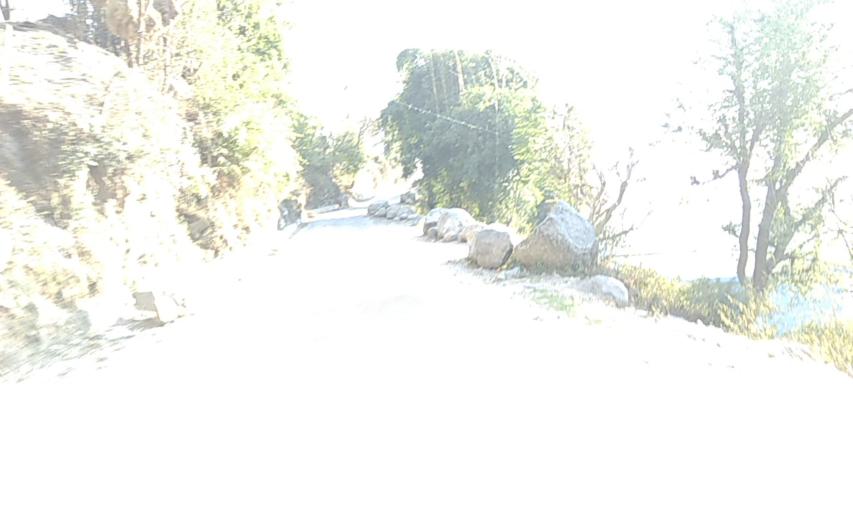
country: IN
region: Himachal Pradesh
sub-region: Kangra
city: Palampur
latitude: 32.1351
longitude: 76.5352
